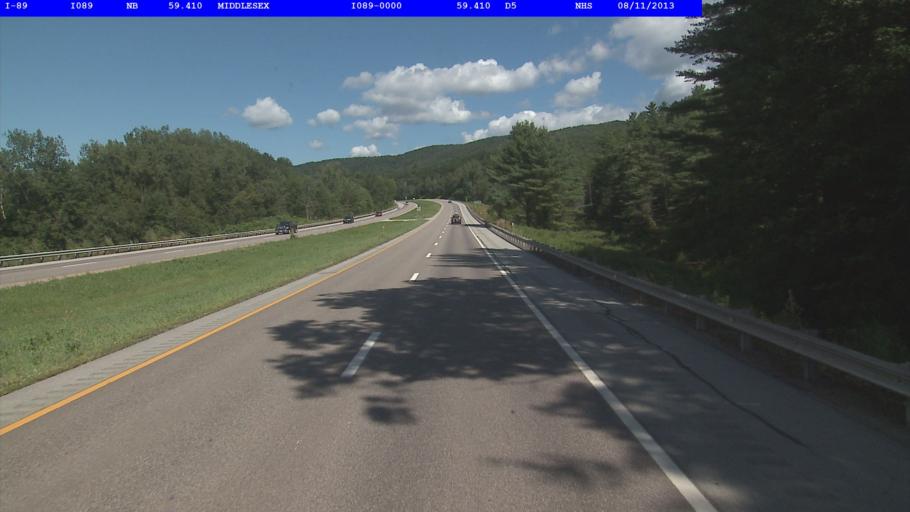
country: US
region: Vermont
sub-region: Washington County
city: Waterbury
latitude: 44.3070
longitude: -72.6914
